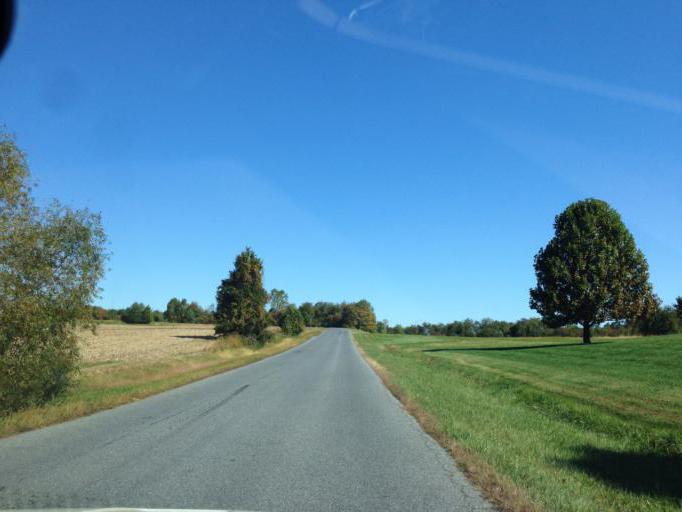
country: US
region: Maryland
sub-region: Howard County
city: Riverside
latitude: 39.1560
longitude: -76.8936
